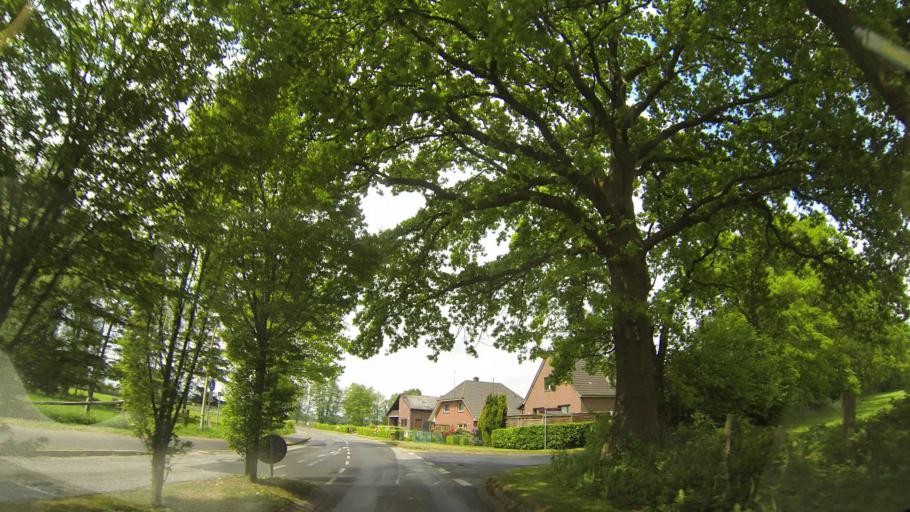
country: DE
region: Schleswig-Holstein
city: Ellerbek
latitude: 53.6610
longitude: 9.8628
